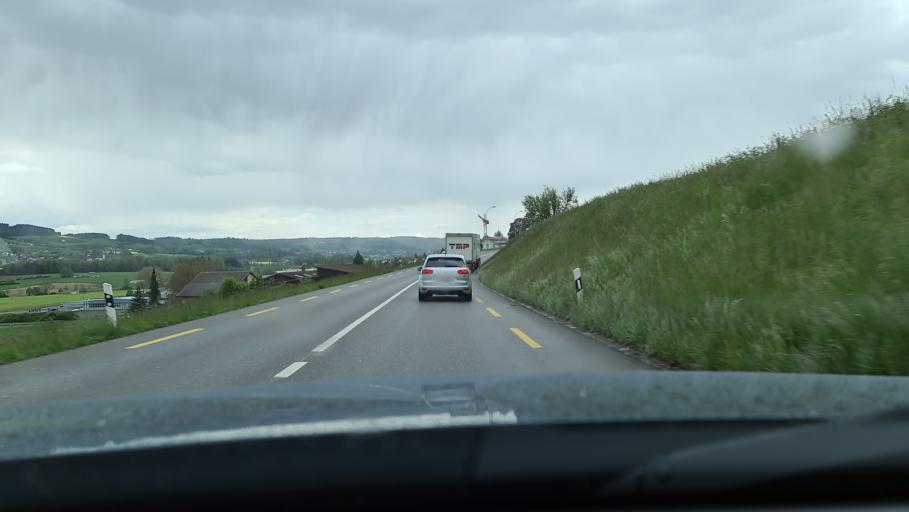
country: CH
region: Lucerne
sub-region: Sursee District
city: Triengen
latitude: 47.2242
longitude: 8.0864
